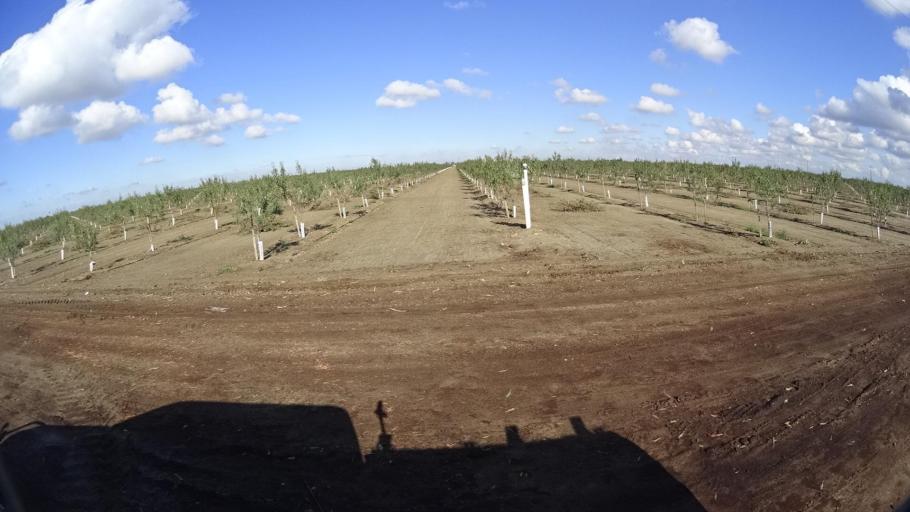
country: US
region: California
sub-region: Kern County
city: McFarland
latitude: 35.6527
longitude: -119.2255
